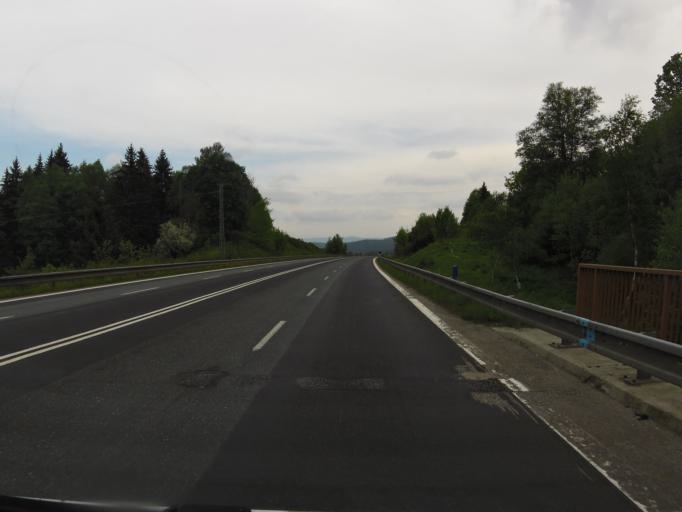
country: DE
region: Bavaria
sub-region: Lower Bavaria
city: Philippsreut
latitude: 48.8976
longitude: 13.7242
